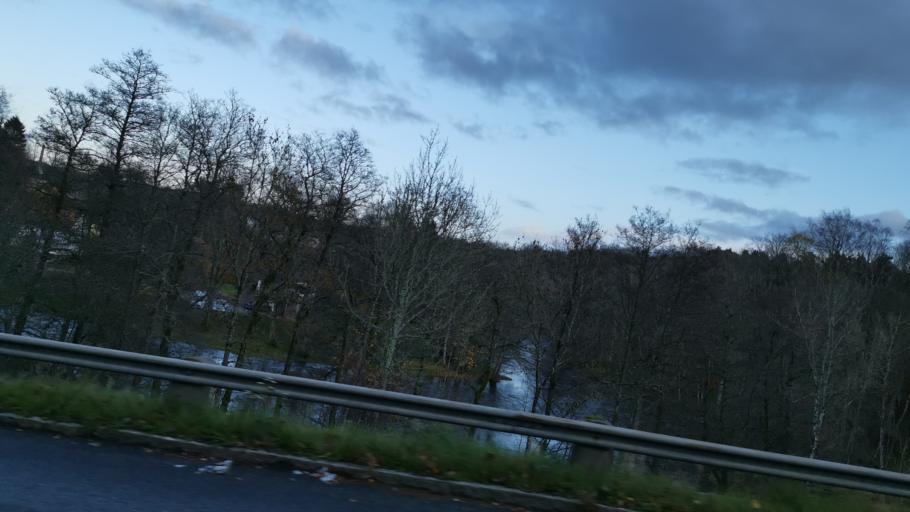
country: SE
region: Vaestra Goetaland
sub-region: Munkedals Kommun
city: Munkedal
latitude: 58.4739
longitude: 11.6748
